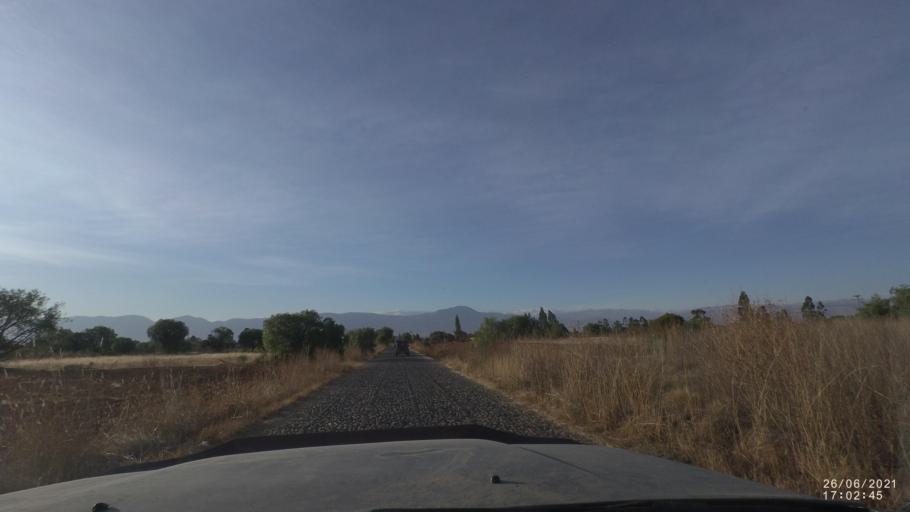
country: BO
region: Cochabamba
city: Cliza
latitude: -17.6507
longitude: -65.9127
